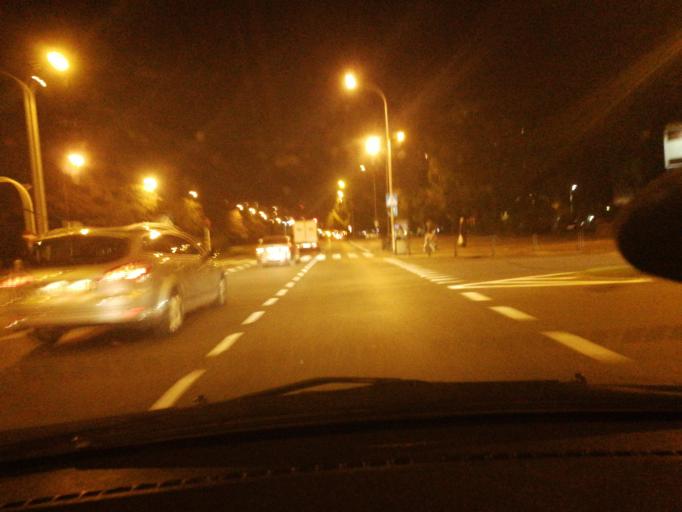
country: PL
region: Masovian Voivodeship
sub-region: Warszawa
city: Targowek
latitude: 52.2927
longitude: 21.0418
